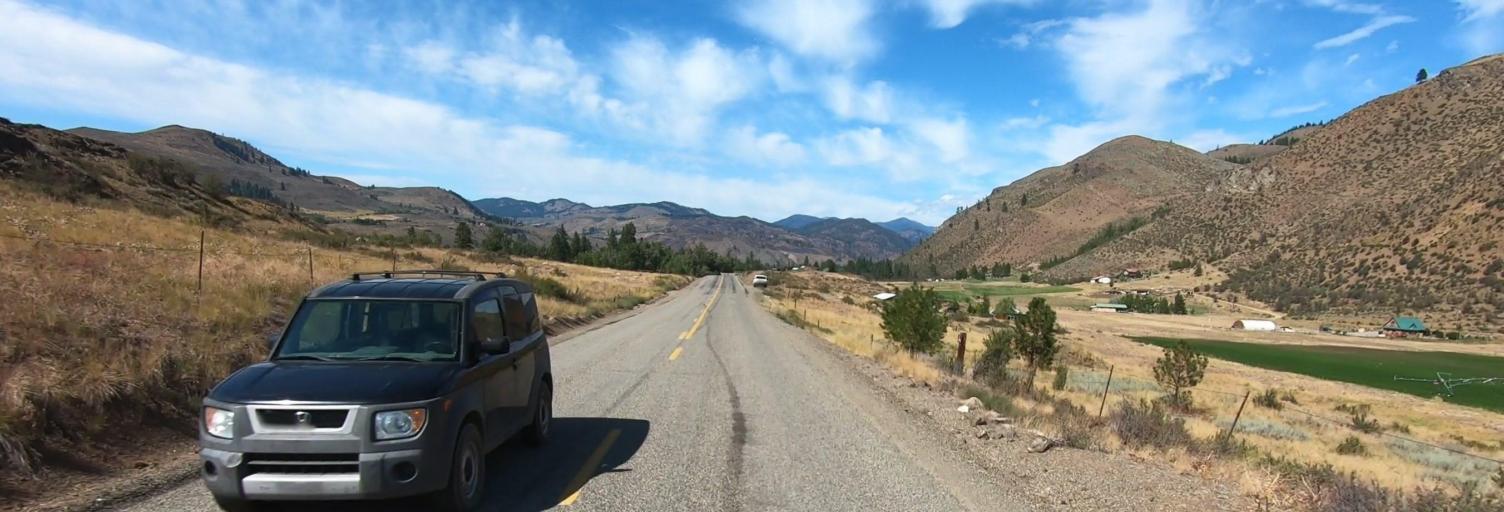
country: US
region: Washington
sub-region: Okanogan County
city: Brewster
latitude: 48.5182
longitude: -120.1760
